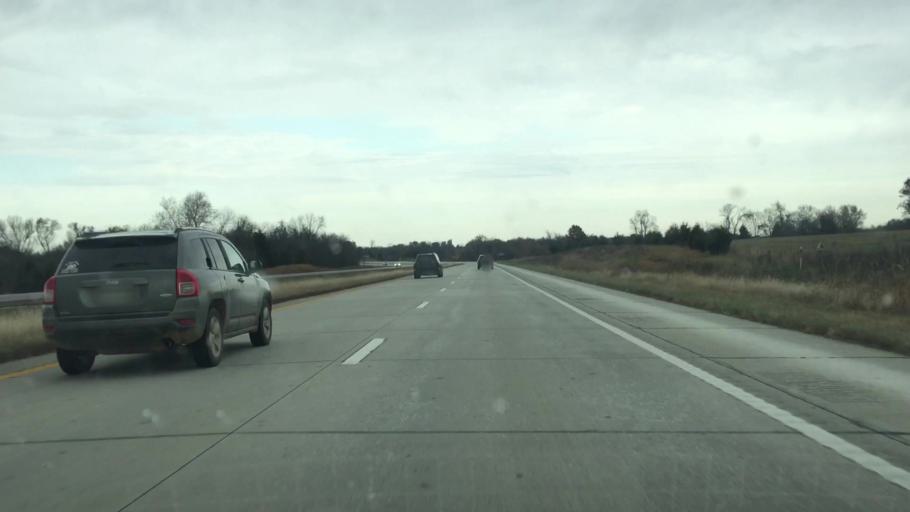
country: US
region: Missouri
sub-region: Saint Clair County
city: Osceola
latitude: 38.1706
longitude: -93.7219
